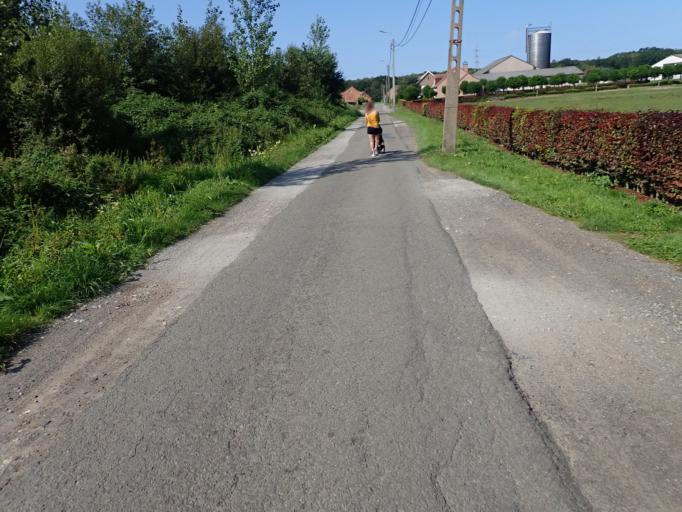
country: BE
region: Flanders
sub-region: Provincie Antwerpen
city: Puurs
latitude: 51.0399
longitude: 4.2820
